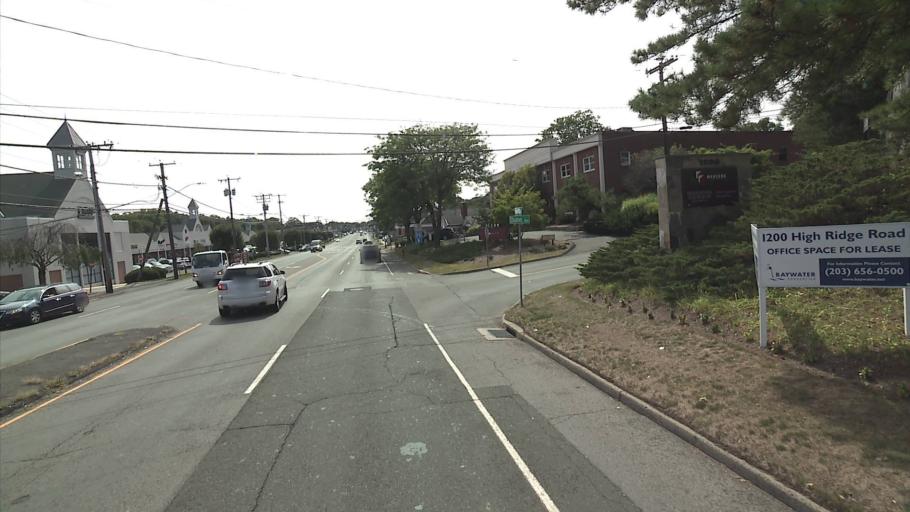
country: US
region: Connecticut
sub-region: Fairfield County
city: North Stamford
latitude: 41.1097
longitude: -73.5472
